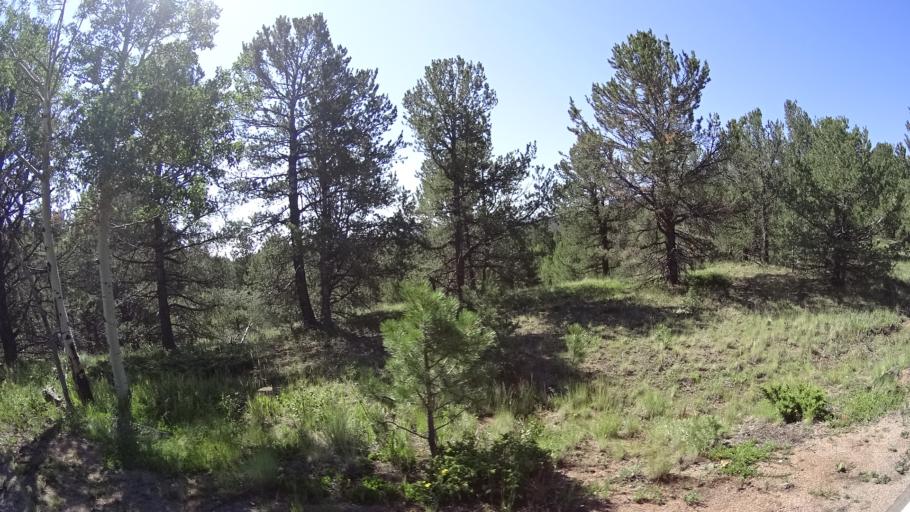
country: US
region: Colorado
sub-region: El Paso County
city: Cascade-Chipita Park
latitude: 38.9144
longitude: -105.0283
